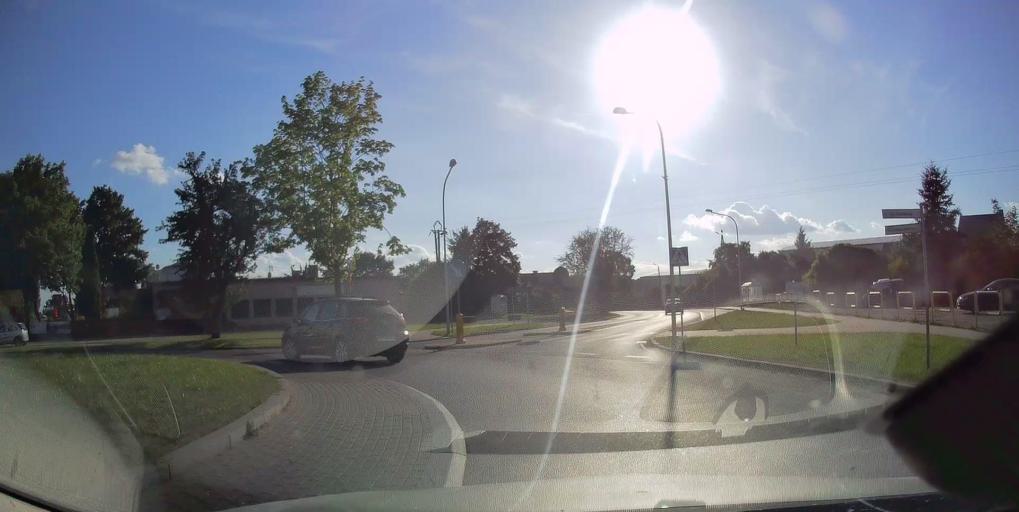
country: PL
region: Masovian Voivodeship
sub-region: Powiat grojecki
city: Belsk Duzy
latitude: 51.8259
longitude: 20.8092
